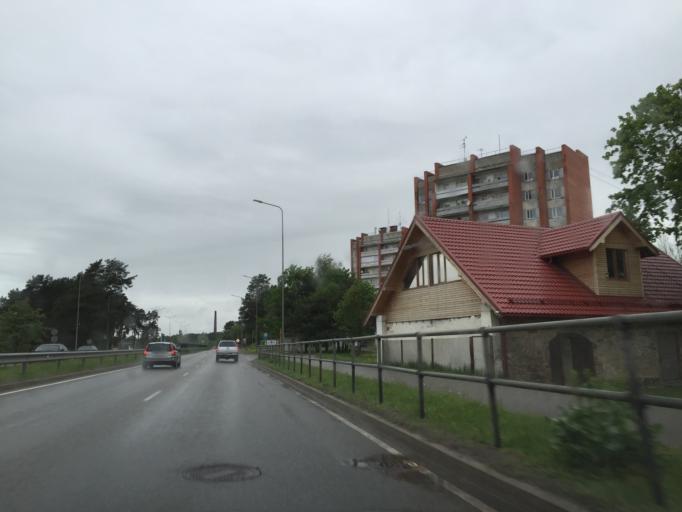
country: LV
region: Ogre
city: Ogre
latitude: 56.8143
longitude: 24.5939
